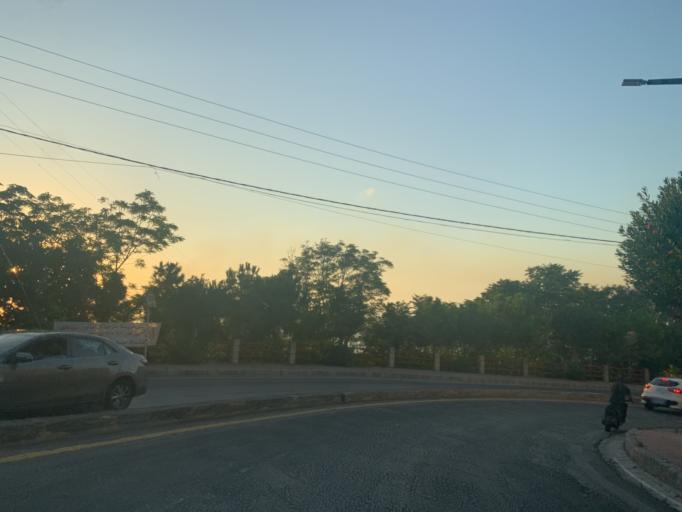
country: LB
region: Mont-Liban
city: Djounie
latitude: 33.9618
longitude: 35.6234
